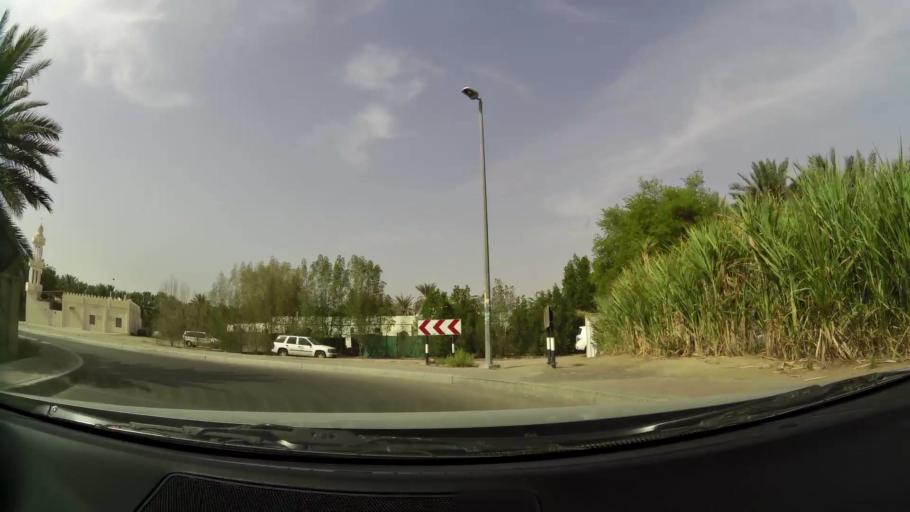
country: AE
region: Abu Dhabi
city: Al Ain
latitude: 24.1531
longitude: 55.7000
